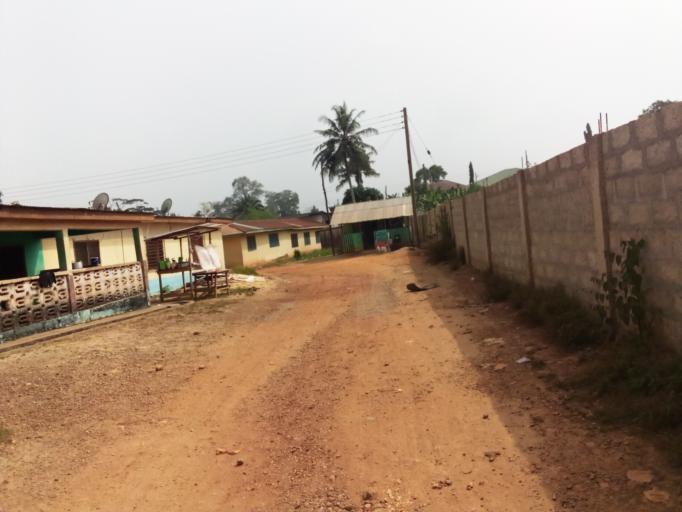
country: CI
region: Sud-Comoe
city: Ayame
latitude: 5.8280
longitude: -2.8195
